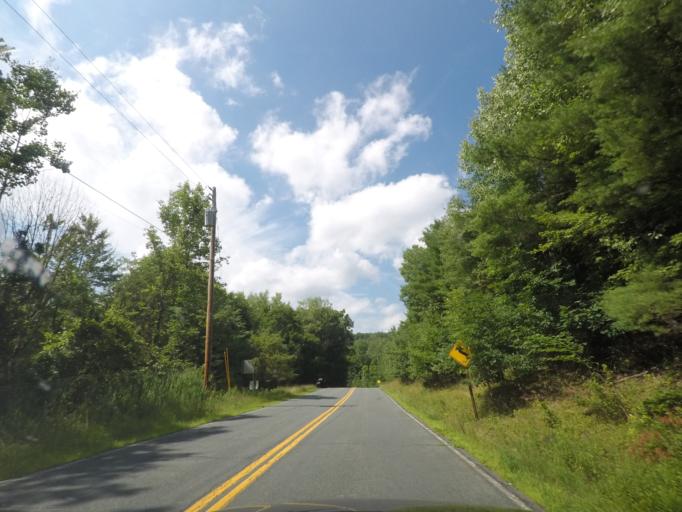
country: US
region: New York
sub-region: Rensselaer County
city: Averill Park
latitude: 42.5992
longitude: -73.5475
